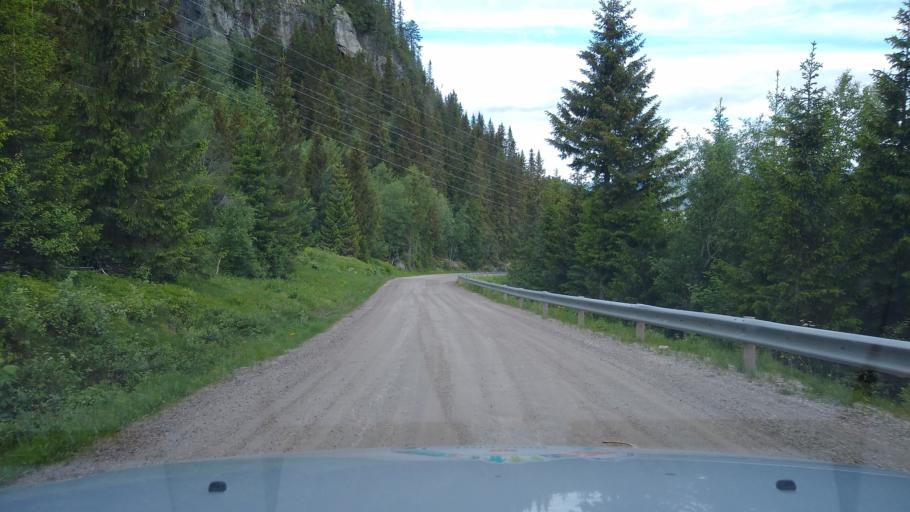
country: NO
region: Oppland
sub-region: Ringebu
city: Ringebu
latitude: 61.4964
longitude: 10.1451
